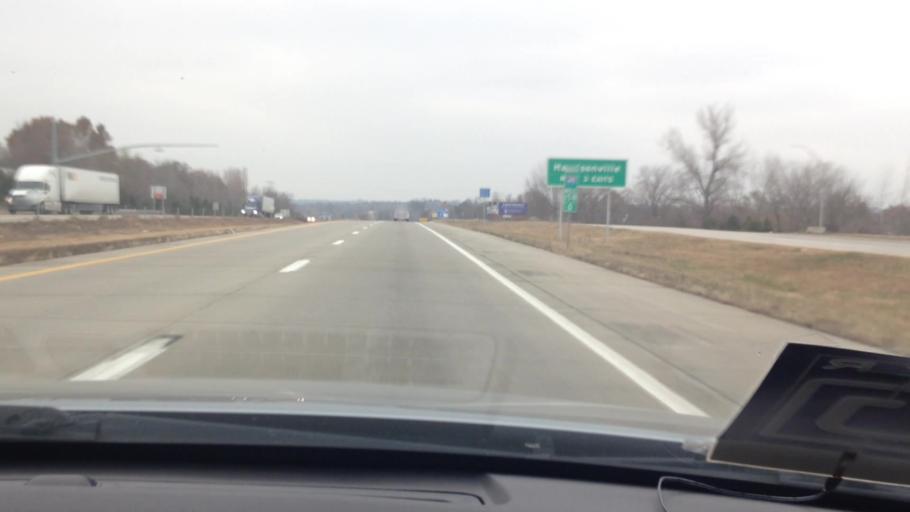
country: US
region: Missouri
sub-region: Cass County
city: Harrisonville
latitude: 38.6280
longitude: -94.3501
